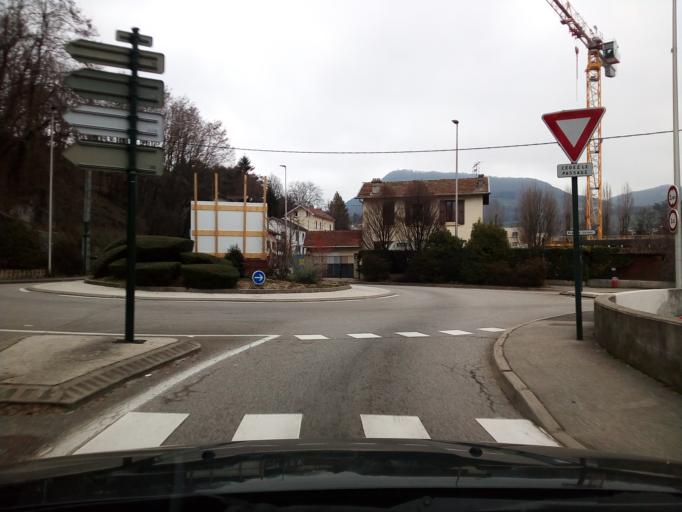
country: FR
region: Rhone-Alpes
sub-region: Departement de l'Isere
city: Voiron
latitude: 45.3540
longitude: 5.5929
